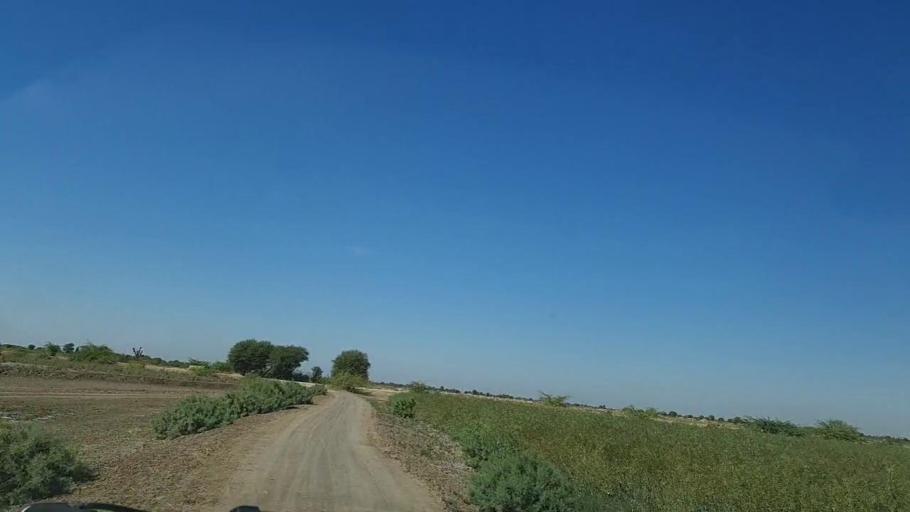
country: PK
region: Sindh
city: Pithoro
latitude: 25.5607
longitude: 69.4594
